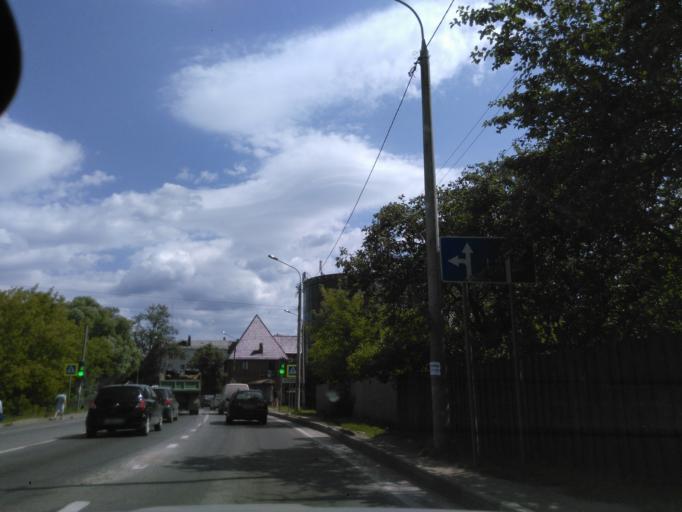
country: RU
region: Moskovskaya
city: Solnechnogorsk
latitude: 56.1901
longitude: 36.9706
